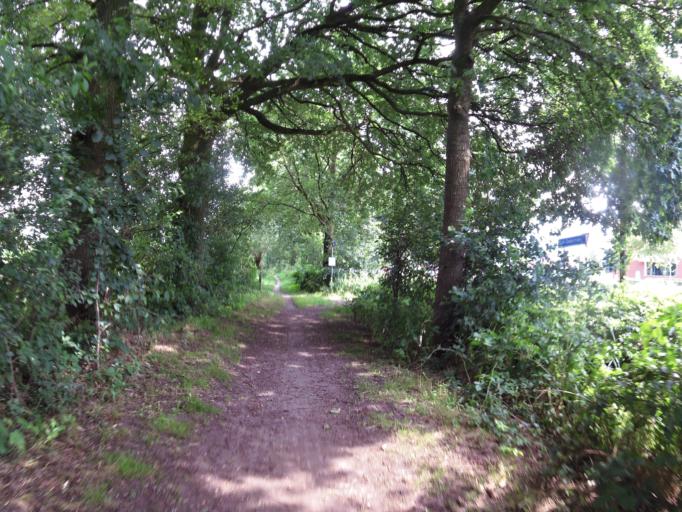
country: NL
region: North Brabant
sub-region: Gemeente Sint-Oedenrode
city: Sint-Oedenrode
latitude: 51.5765
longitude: 5.4677
